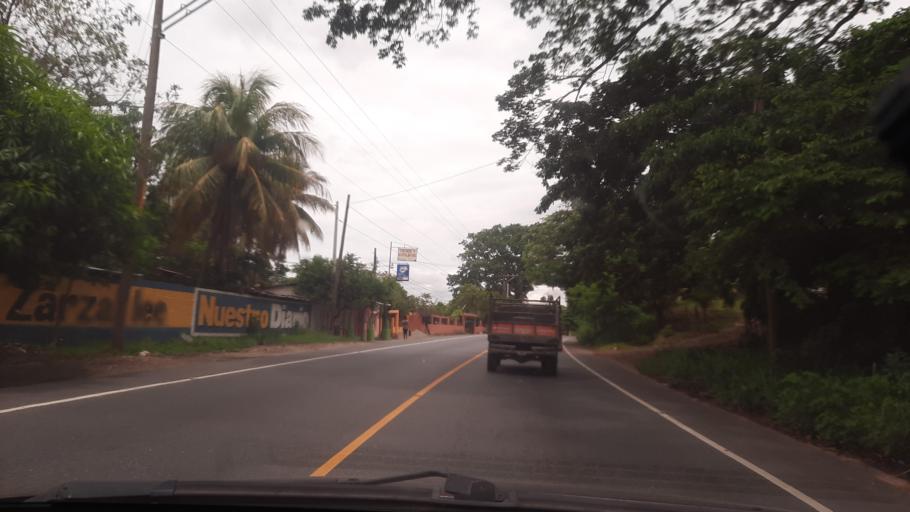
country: GT
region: Zacapa
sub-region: Municipio de Zacapa
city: Gualan
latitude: 15.1442
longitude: -89.3285
